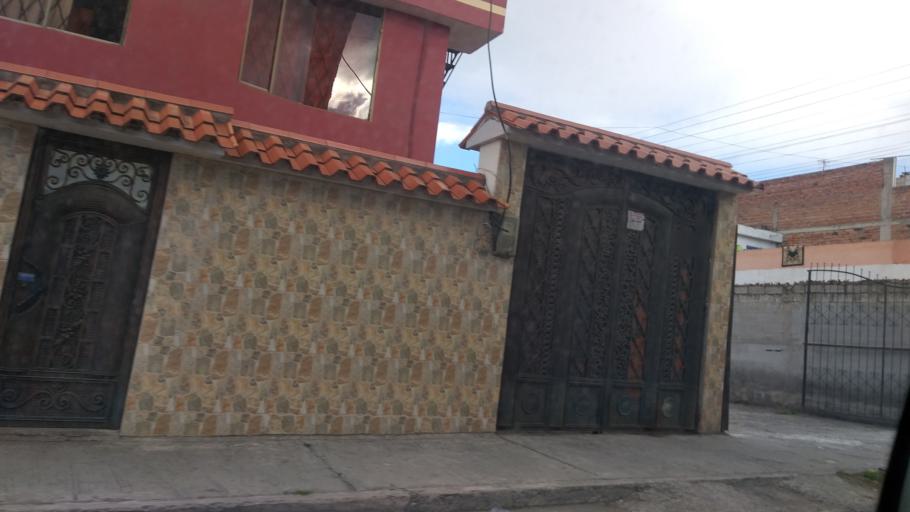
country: EC
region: Chimborazo
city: Riobamba
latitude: -1.6870
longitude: -78.6349
